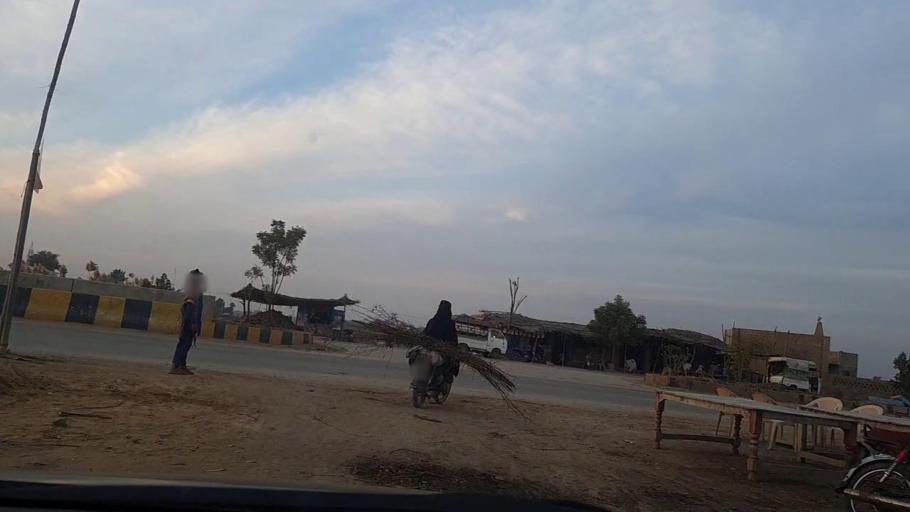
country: PK
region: Sindh
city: Sakrand
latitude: 26.2103
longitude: 68.3250
